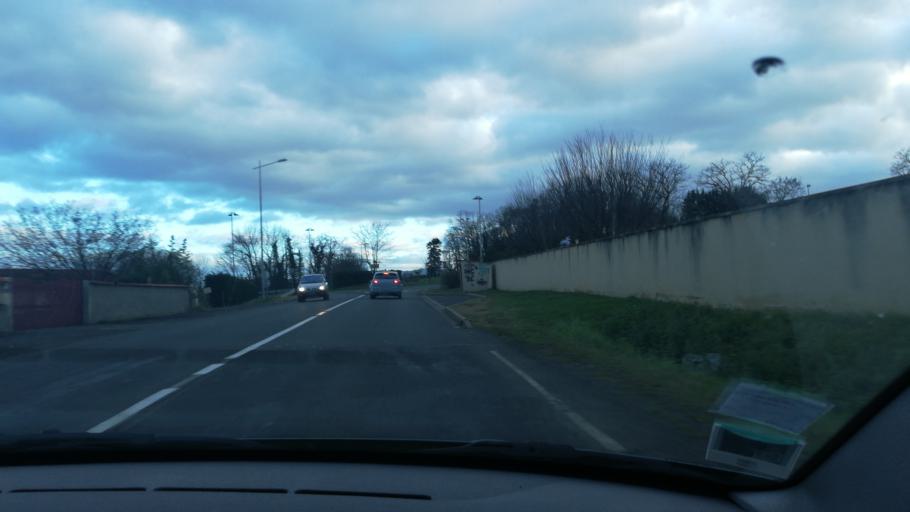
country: FR
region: Auvergne
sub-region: Departement du Puy-de-Dome
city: Vertaizon
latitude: 45.7723
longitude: 3.2958
